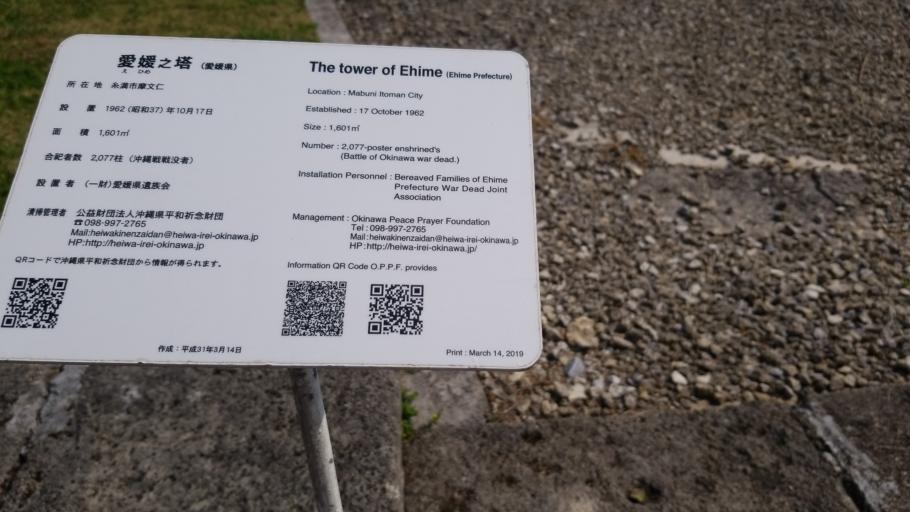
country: JP
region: Okinawa
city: Itoman
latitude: 26.0933
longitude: 127.7249
